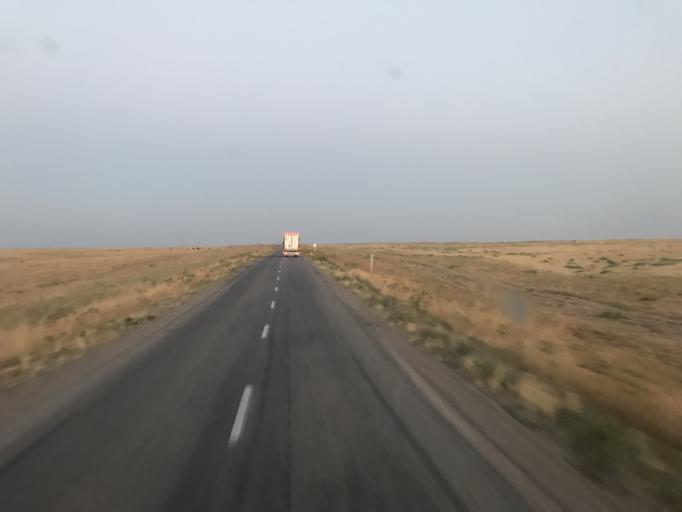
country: UZ
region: Toshkent
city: Chinoz
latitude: 41.1708
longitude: 68.6403
